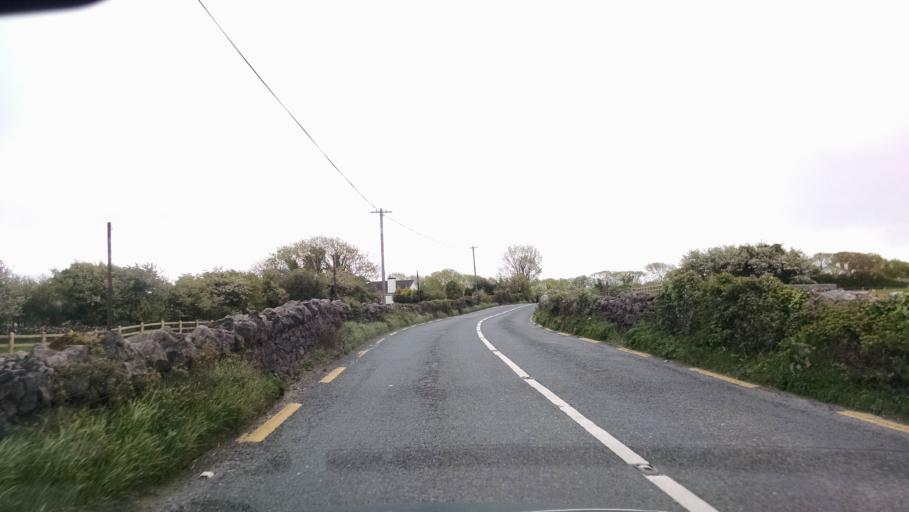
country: IE
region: Connaught
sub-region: County Galway
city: Moycullen
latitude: 53.4375
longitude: -9.0633
